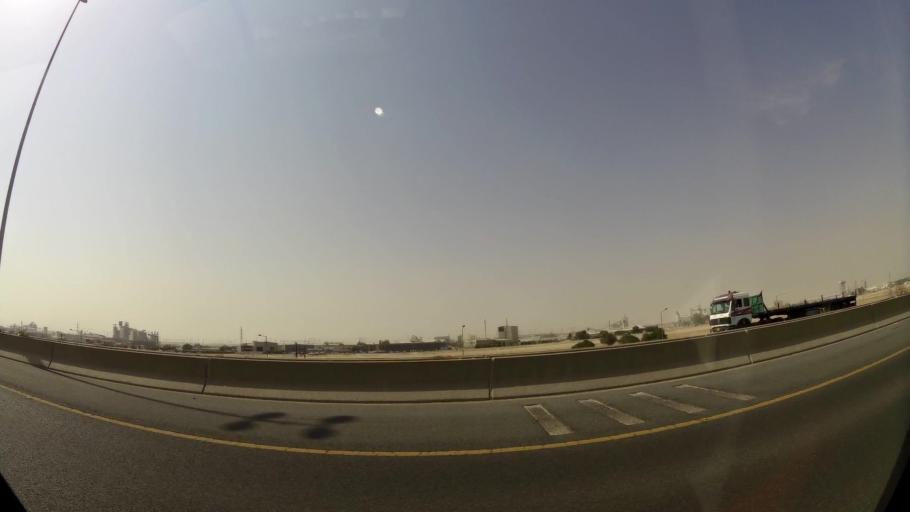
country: KW
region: Al Ahmadi
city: Al Fahahil
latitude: 29.0126
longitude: 48.1318
